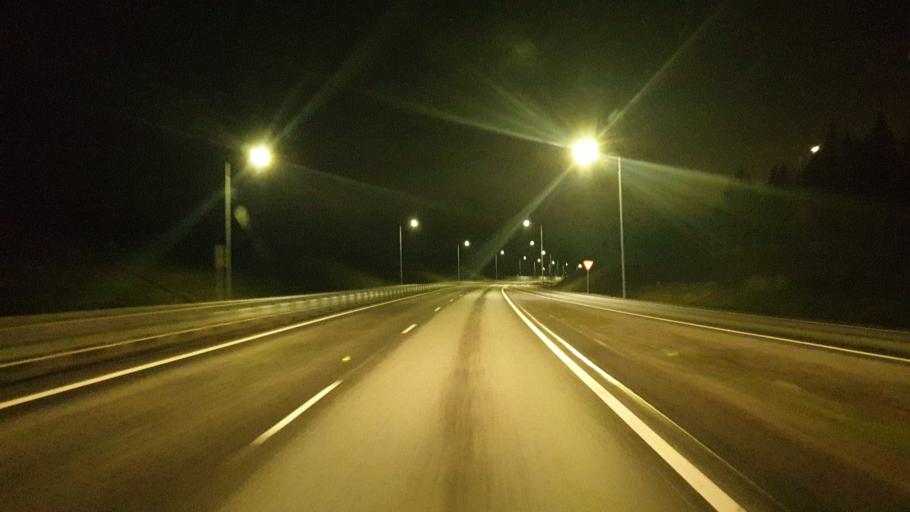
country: FI
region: Central Finland
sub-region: AEaenekoski
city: AEaenekoski
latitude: 62.5711
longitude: 25.6737
